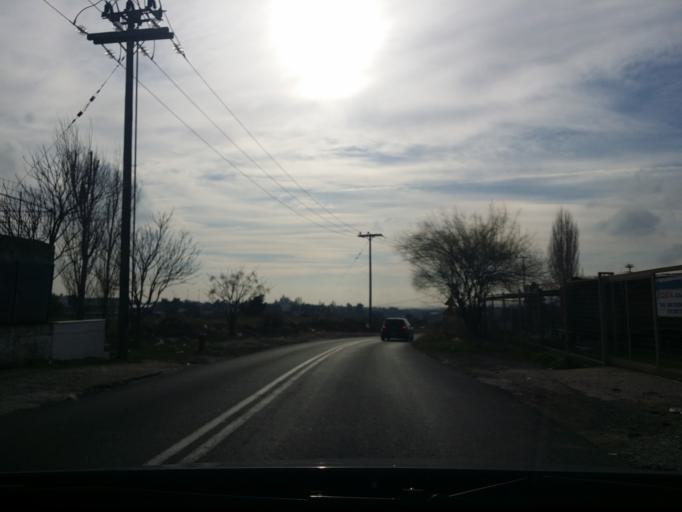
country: GR
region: Attica
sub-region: Nomarchia Athinas
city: Metamorfosi
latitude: 38.0791
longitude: 23.7633
